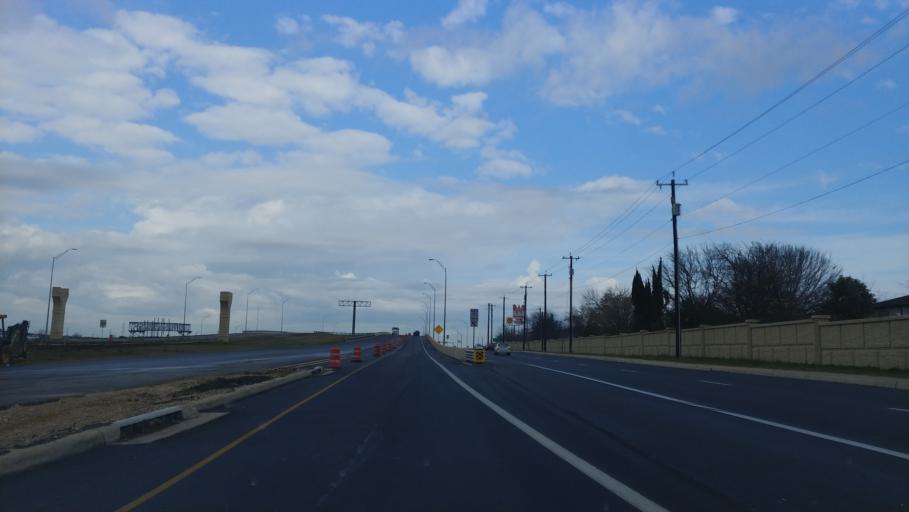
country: US
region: Texas
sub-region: Bexar County
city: Lackland Air Force Base
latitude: 29.3999
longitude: -98.7042
